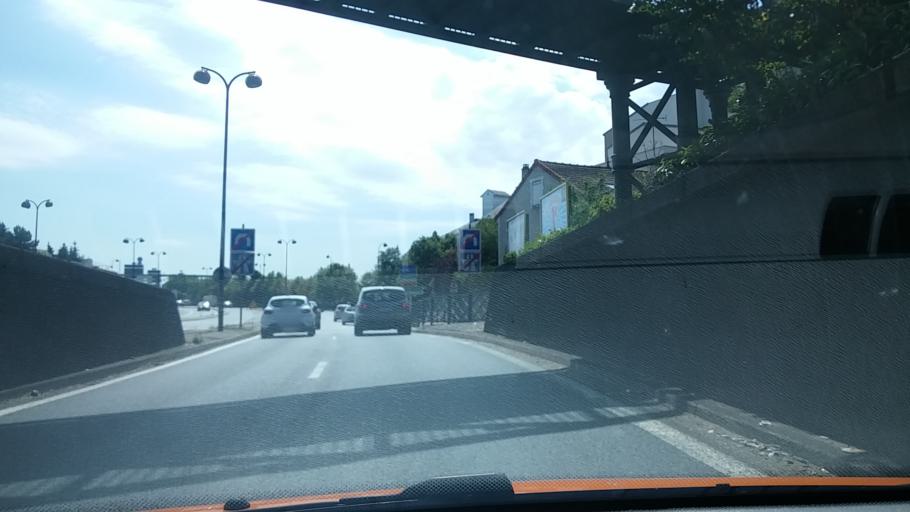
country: FR
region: Ile-de-France
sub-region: Departement du Val-de-Marne
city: Nogent-sur-Marne
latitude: 48.8345
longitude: 2.4932
